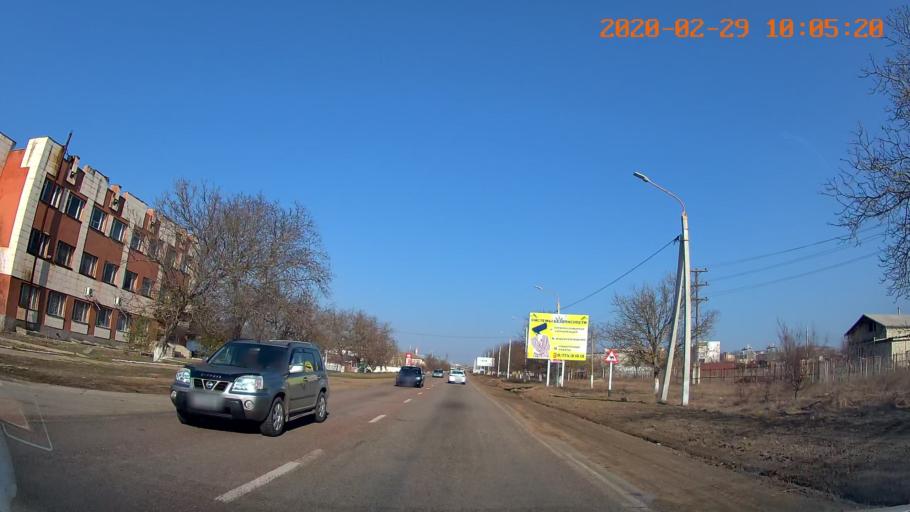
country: MD
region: Telenesti
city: Tiraspolul Nou
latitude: 46.8063
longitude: 29.6720
